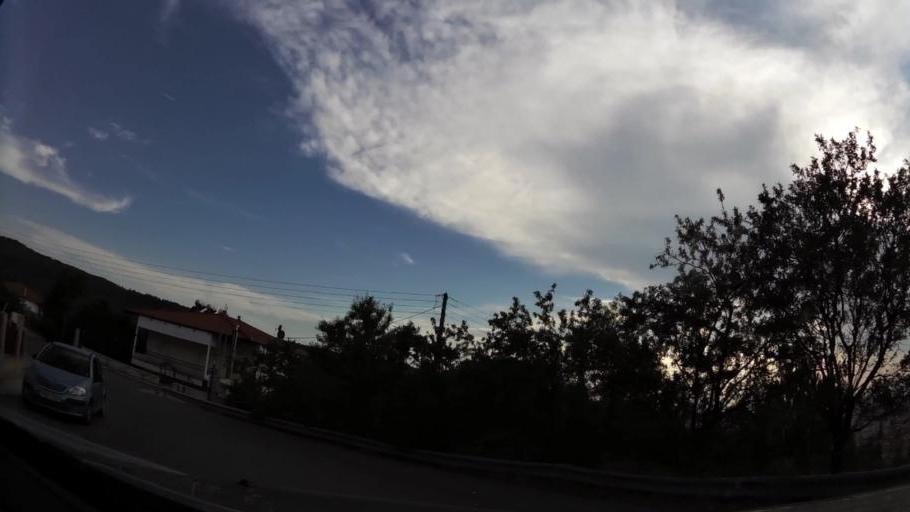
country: GR
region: Central Macedonia
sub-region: Nomos Thessalonikis
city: Pefka
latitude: 40.6603
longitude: 22.9946
